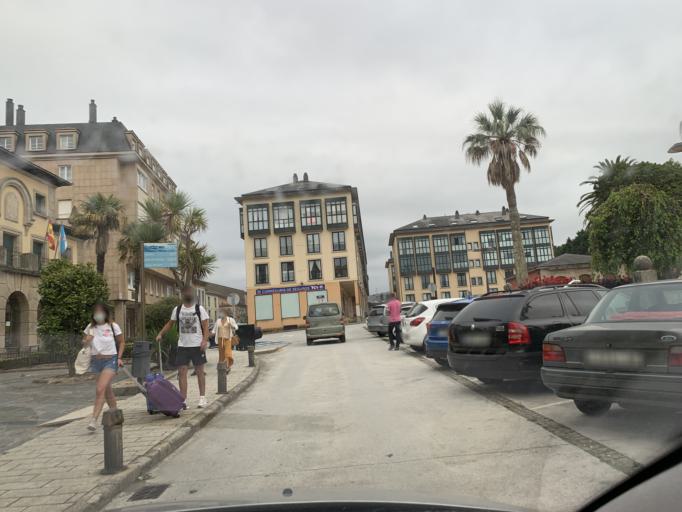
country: ES
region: Galicia
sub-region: Provincia de Lugo
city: Ribadeo
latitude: 43.5362
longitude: -7.0396
